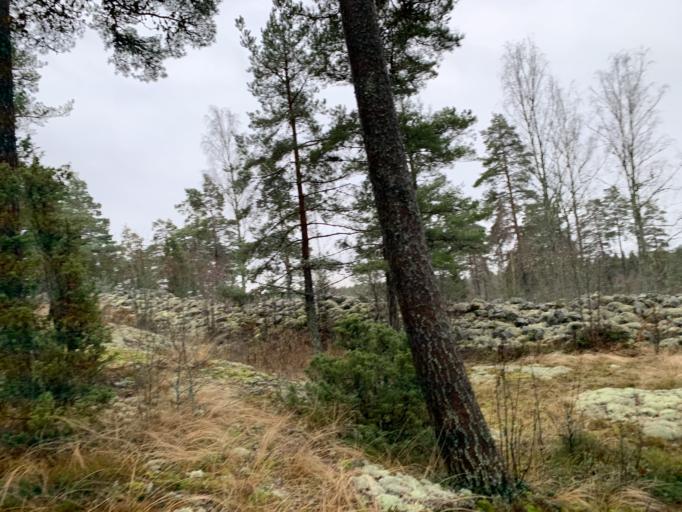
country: SE
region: Soedermanland
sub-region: Eskilstuna Kommun
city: Kvicksund
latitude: 59.3689
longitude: 16.2863
